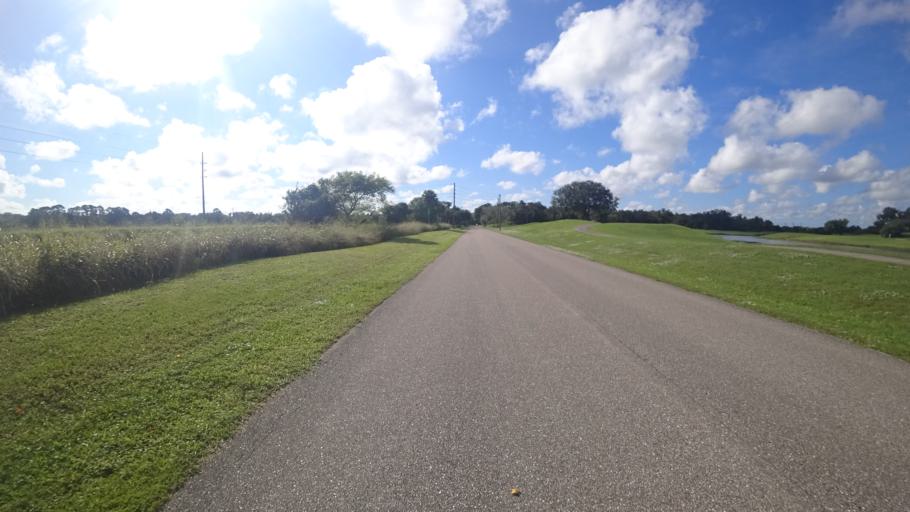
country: US
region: Florida
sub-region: Manatee County
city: Ellenton
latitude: 27.5777
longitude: -82.4747
